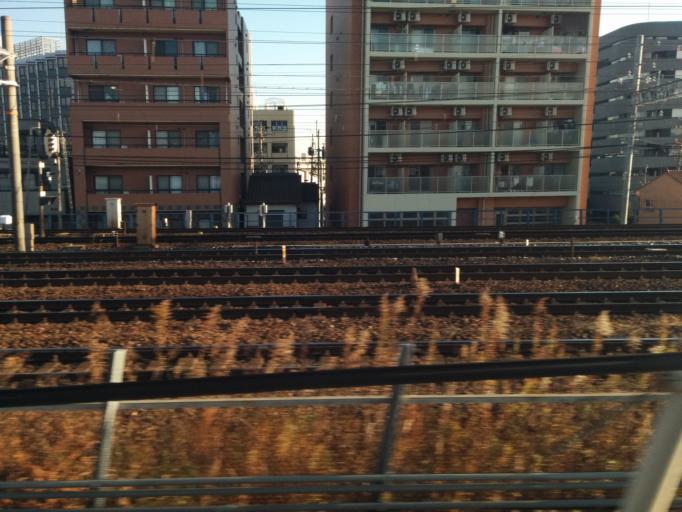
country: JP
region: Aichi
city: Nagoya-shi
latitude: 35.1828
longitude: 136.8736
